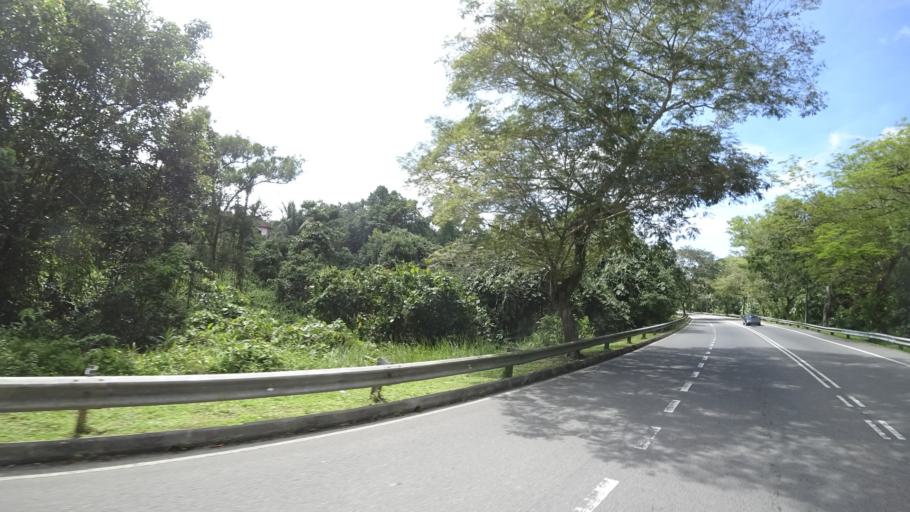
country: BN
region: Brunei and Muara
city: Bandar Seri Begawan
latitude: 4.8750
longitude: 114.8992
